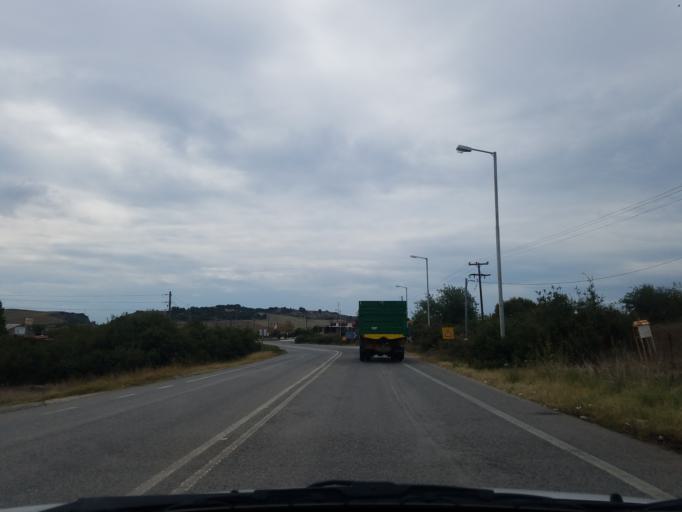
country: GR
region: Central Greece
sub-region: Nomos Fthiotidos
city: Domokos
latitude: 39.1129
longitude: 22.3090
